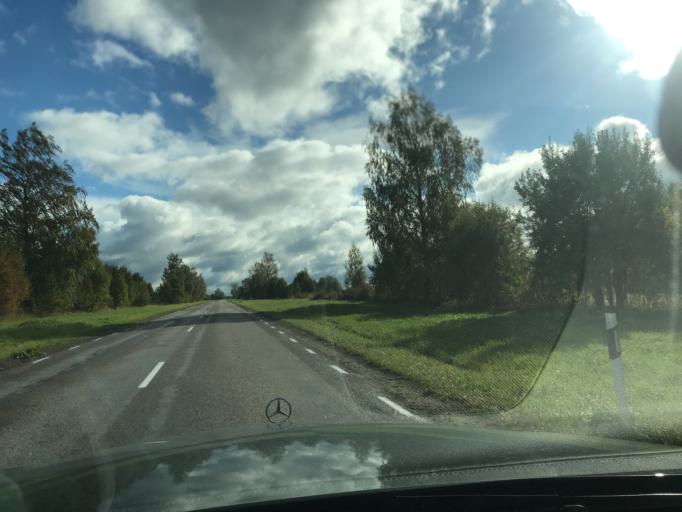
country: EE
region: Valgamaa
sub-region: Torva linn
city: Torva
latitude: 58.0110
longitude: 26.1838
